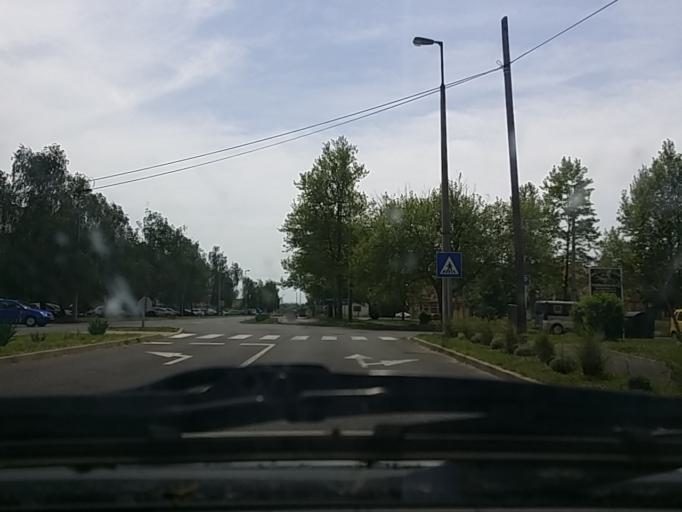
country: HU
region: Somogy
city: Barcs
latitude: 45.9616
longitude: 17.4665
